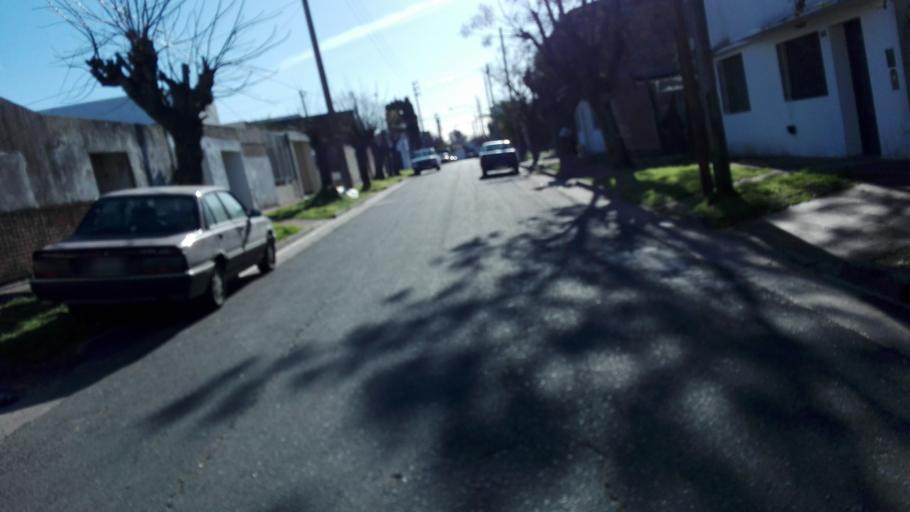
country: AR
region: Buenos Aires
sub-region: Partido de La Plata
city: La Plata
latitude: -34.8867
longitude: -57.9941
